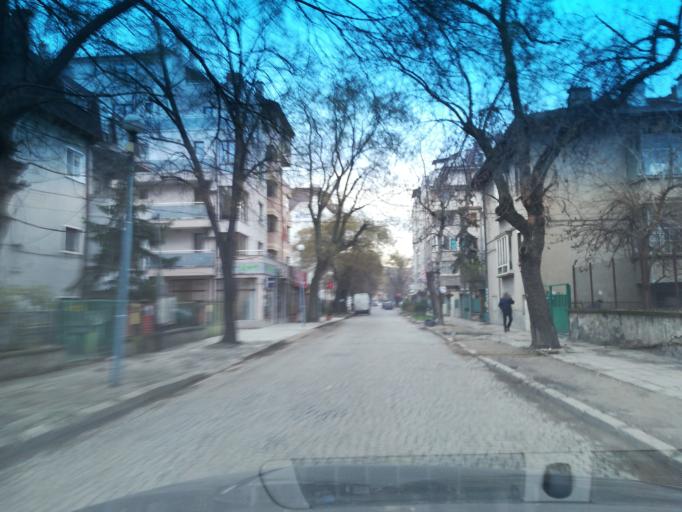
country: BG
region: Plovdiv
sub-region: Obshtina Plovdiv
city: Plovdiv
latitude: 42.1372
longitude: 24.7596
